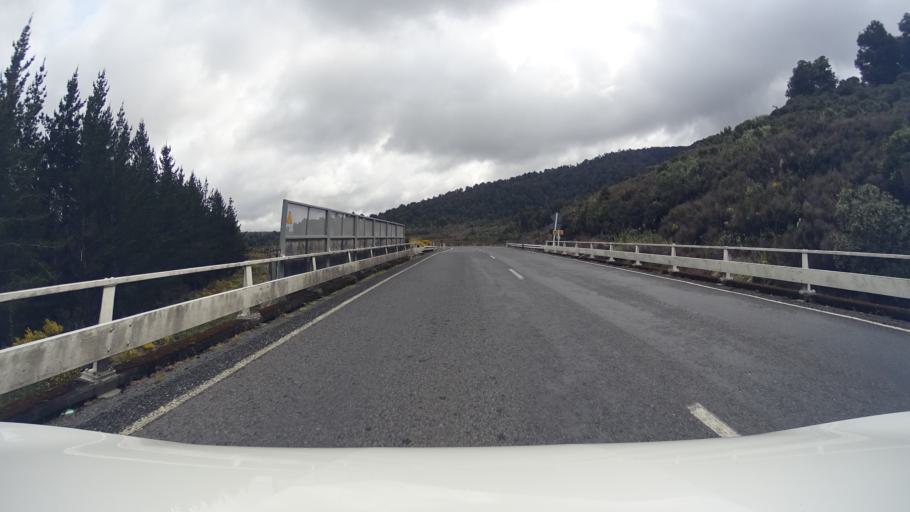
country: NZ
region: Manawatu-Wanganui
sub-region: Ruapehu District
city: Waiouru
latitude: -39.2227
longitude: 175.3986
